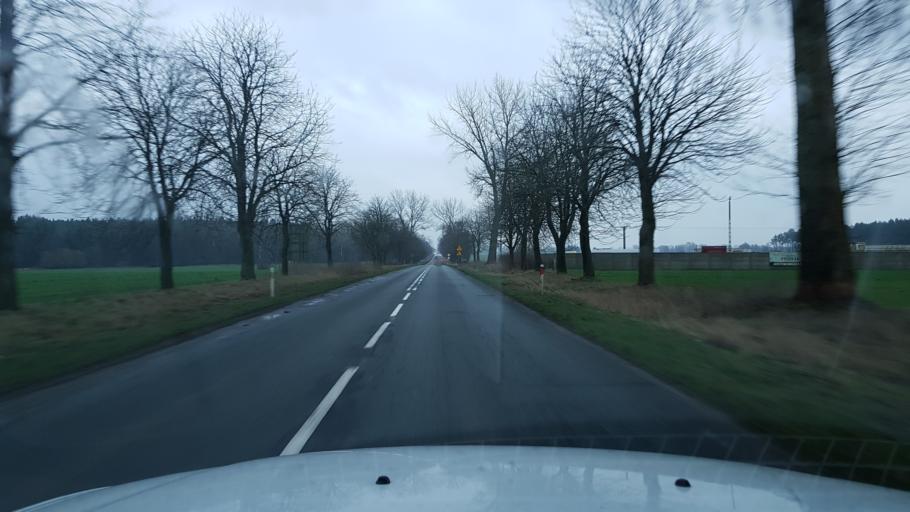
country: PL
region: West Pomeranian Voivodeship
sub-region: Powiat gryficki
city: Gryfice
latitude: 53.8984
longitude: 15.2044
